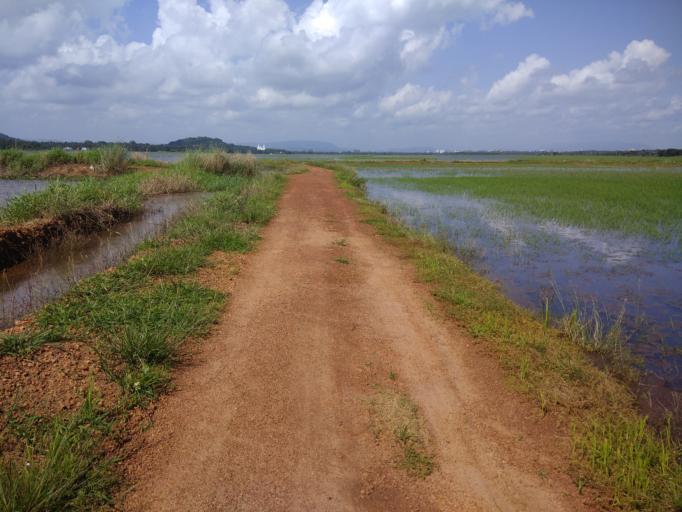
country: IN
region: Kerala
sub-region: Thrissur District
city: Trichur
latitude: 10.5343
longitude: 76.1479
